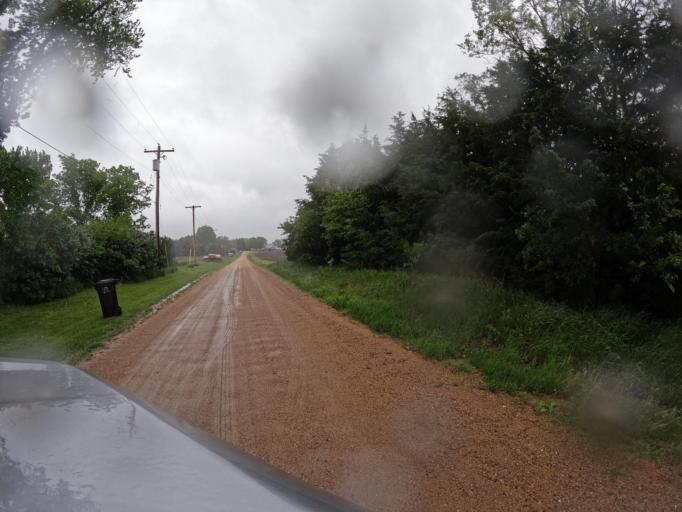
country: US
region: Nebraska
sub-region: Gage County
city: Wymore
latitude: 40.1283
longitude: -96.6574
